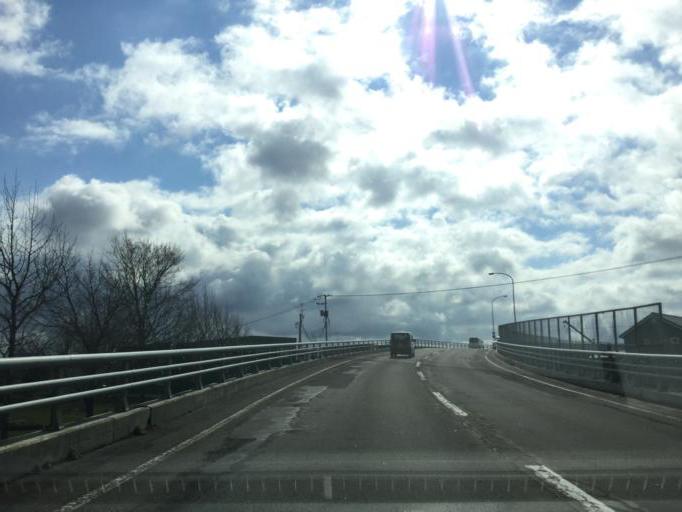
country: JP
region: Hokkaido
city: Iwamizawa
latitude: 43.2085
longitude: 141.7639
